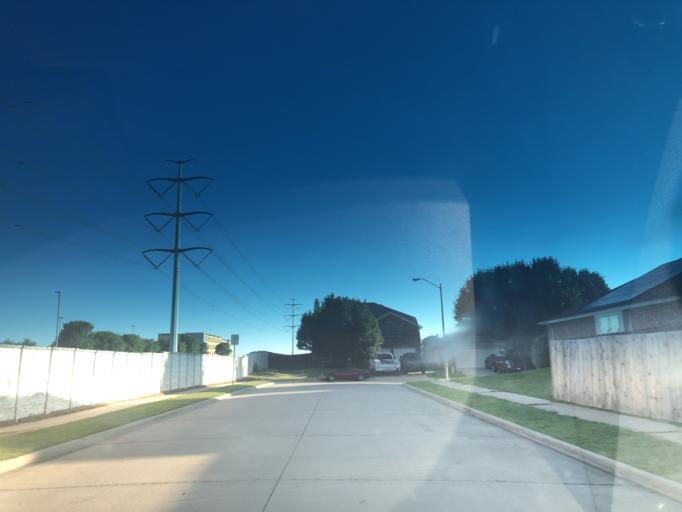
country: US
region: Texas
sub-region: Dallas County
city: Grand Prairie
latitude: 32.7013
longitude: -97.0222
